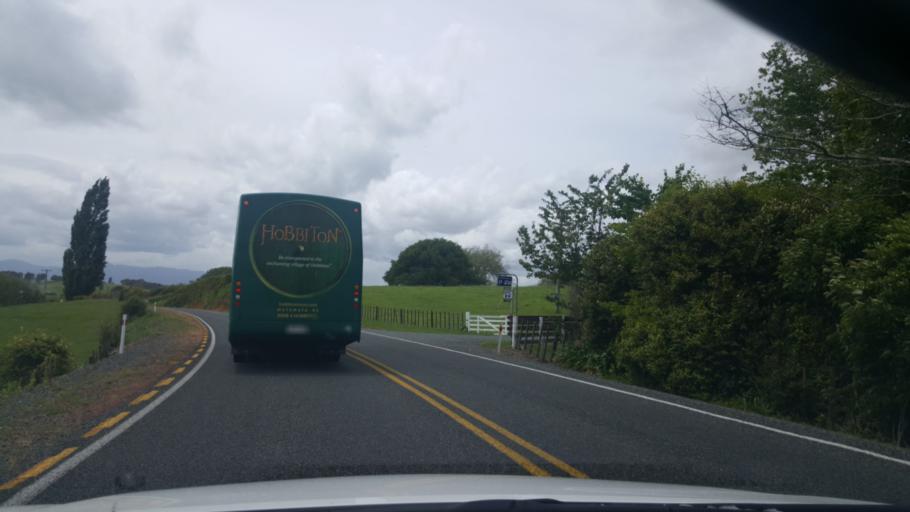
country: NZ
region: Waikato
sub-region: Matamata-Piako District
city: Matamata
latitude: -37.8802
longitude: 175.6972
